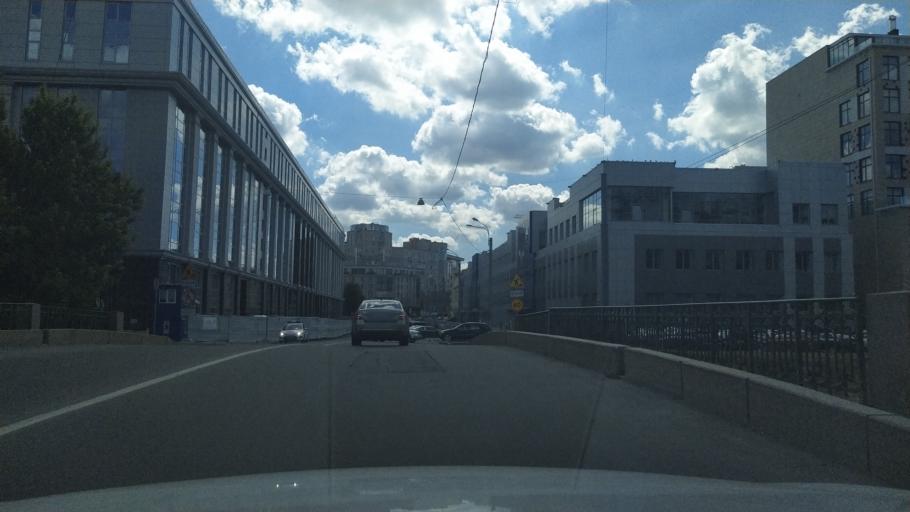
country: RU
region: St.-Petersburg
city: Novaya Derevnya
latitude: 59.9689
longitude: 30.2885
